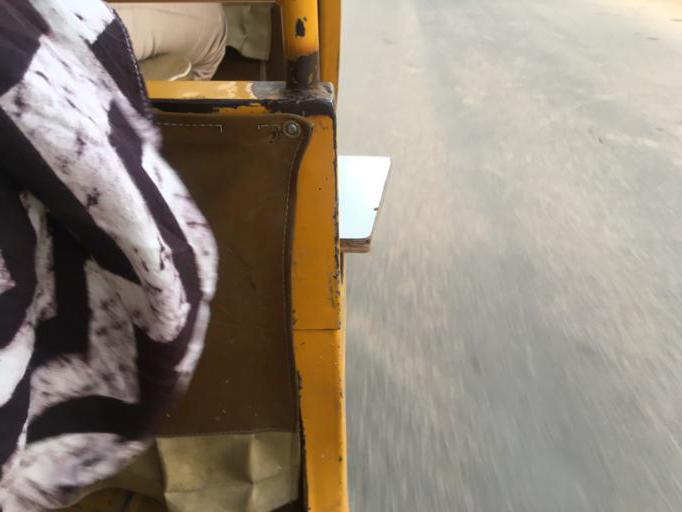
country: IN
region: Telangana
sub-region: Medak
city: Serilingampalle
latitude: 17.4327
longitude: 78.3341
